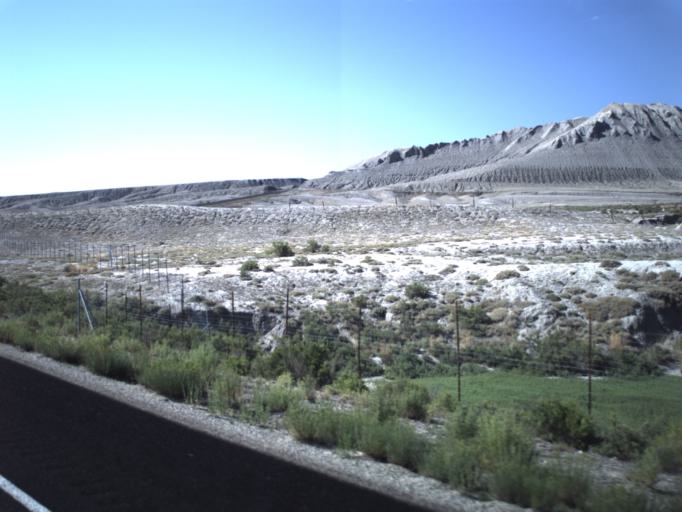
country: US
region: Utah
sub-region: Emery County
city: Ferron
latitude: 39.0528
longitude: -111.1237
